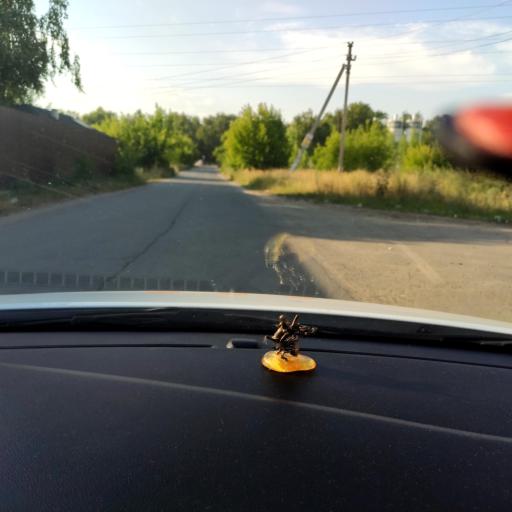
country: RU
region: Tatarstan
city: Staroye Arakchino
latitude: 55.8111
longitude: 48.9133
